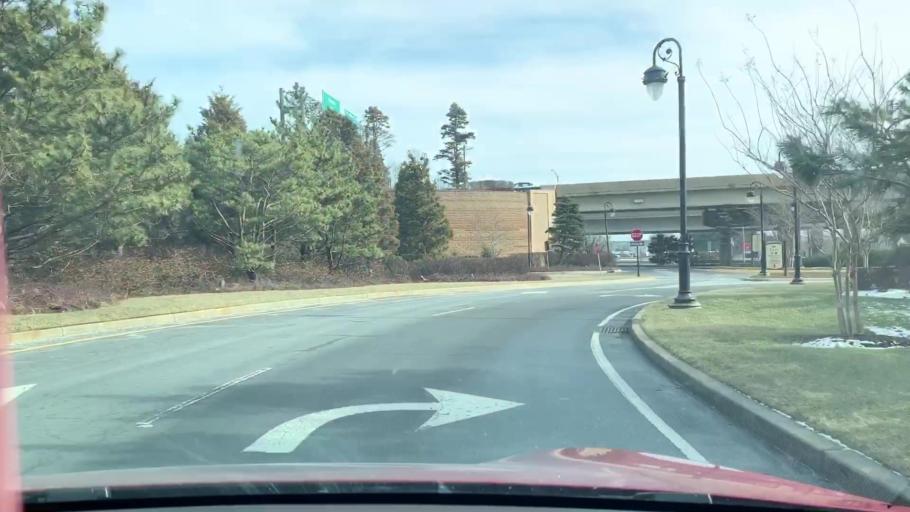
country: US
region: New Jersey
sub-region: Atlantic County
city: Atlantic City
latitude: 39.3779
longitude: -74.4328
